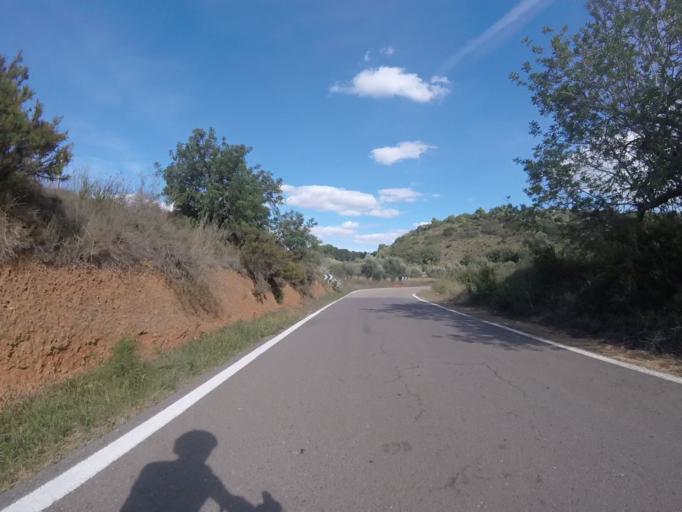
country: ES
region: Valencia
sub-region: Provincia de Castello
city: Cuevas de Vinroma
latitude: 40.3691
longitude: 0.1209
